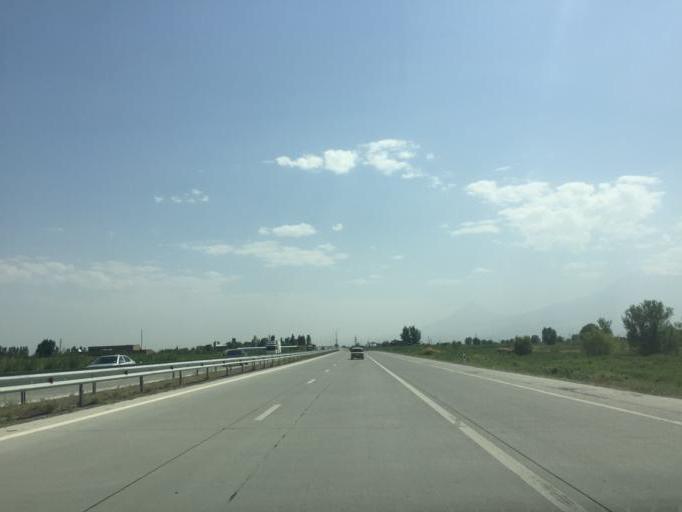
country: AM
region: Ararat
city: Arevabuyr
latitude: 40.0307
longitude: 44.4634
